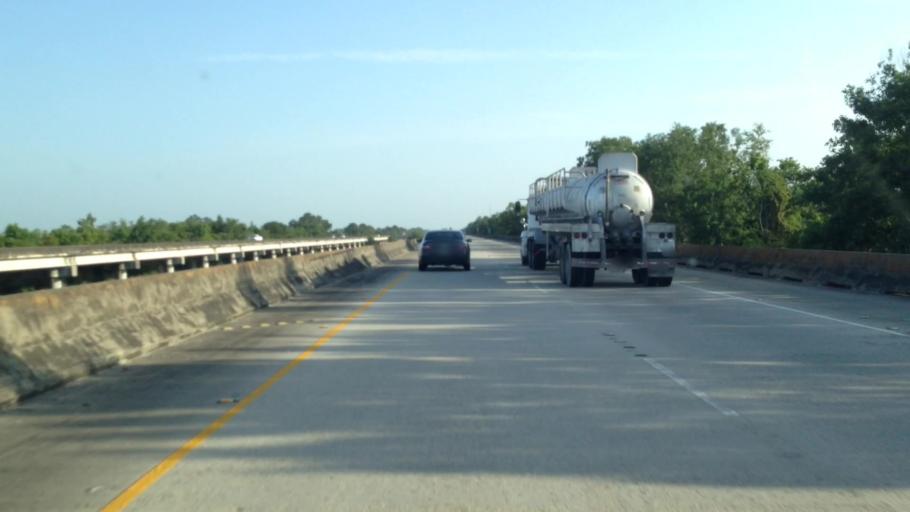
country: US
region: Louisiana
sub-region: Tangipahoa Parish
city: Ponchatoula
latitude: 30.3447
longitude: -90.4141
